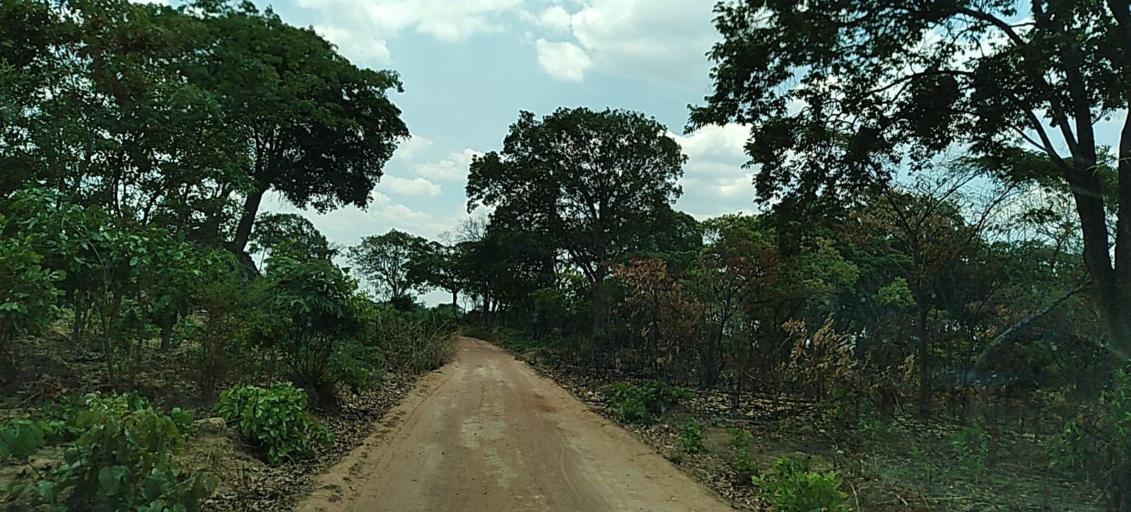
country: ZM
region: Copperbelt
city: Chililabombwe
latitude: -12.3920
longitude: 27.9208
